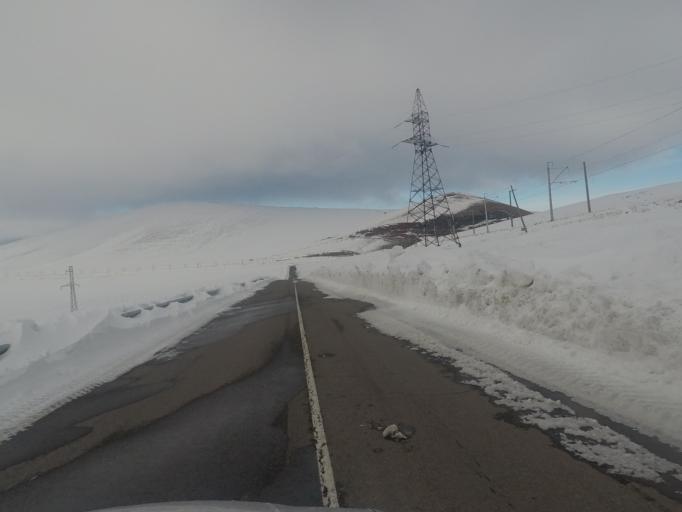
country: GE
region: Kvemo Kartli
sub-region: Tsalka
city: Tsalka
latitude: 41.4566
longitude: 43.8553
